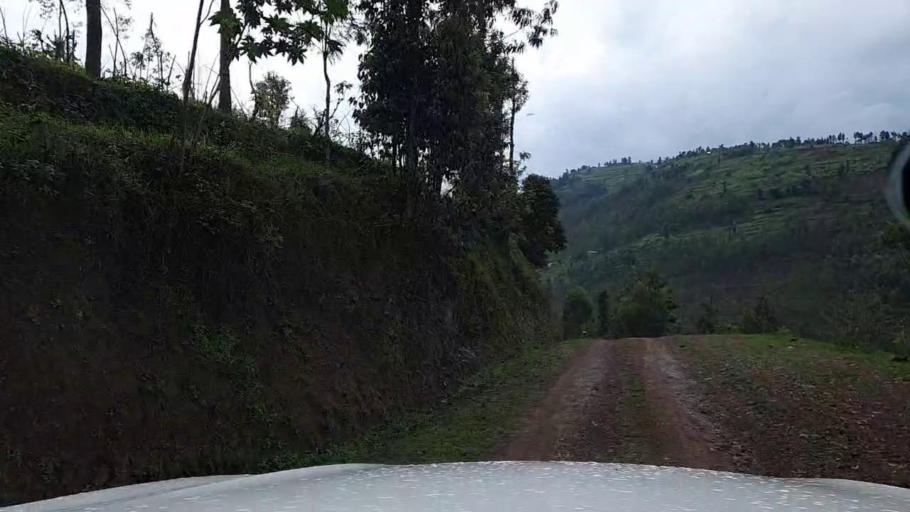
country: RW
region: Northern Province
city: Byumba
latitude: -1.7200
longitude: 29.9161
